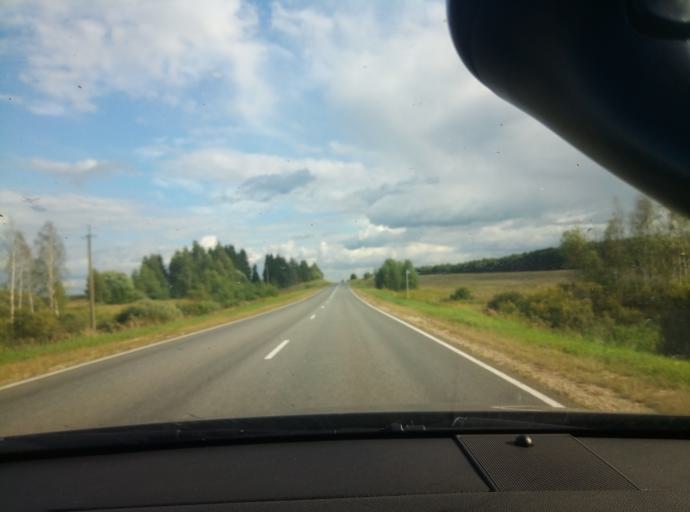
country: RU
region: Kaluga
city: Yukhnov
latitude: 54.6161
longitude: 35.3531
